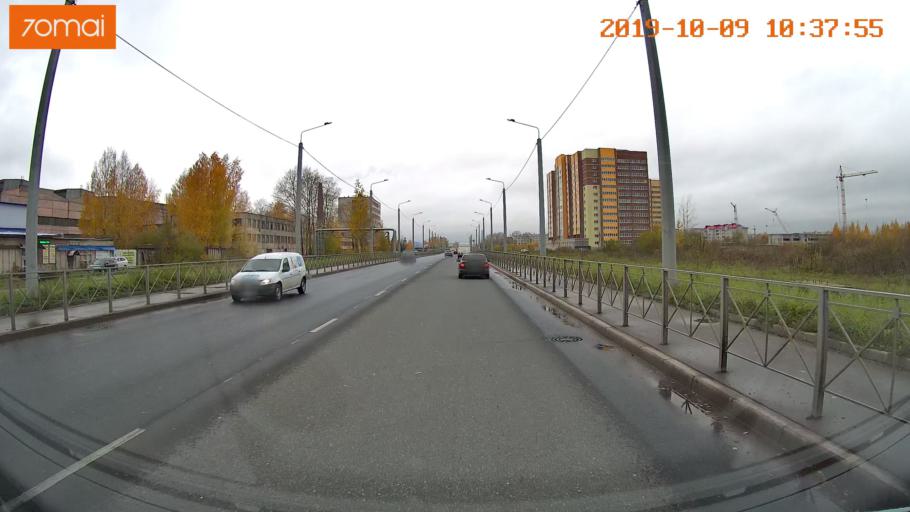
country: RU
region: Vologda
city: Vologda
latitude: 59.2358
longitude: 39.8539
